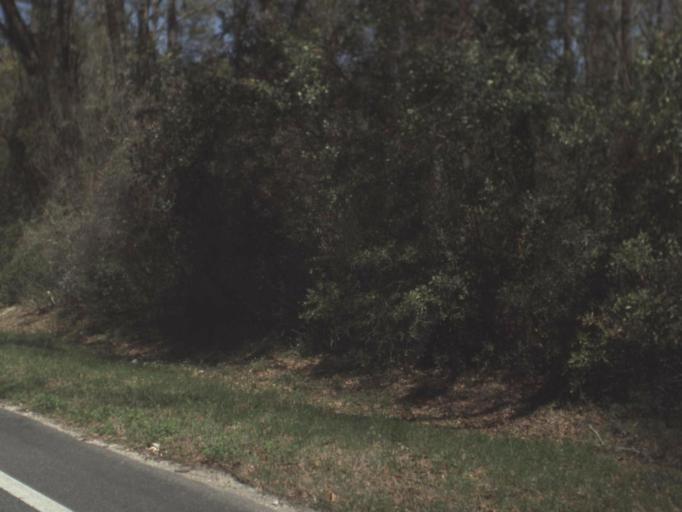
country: US
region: Florida
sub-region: Leon County
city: Woodville
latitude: 30.2769
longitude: -84.2395
